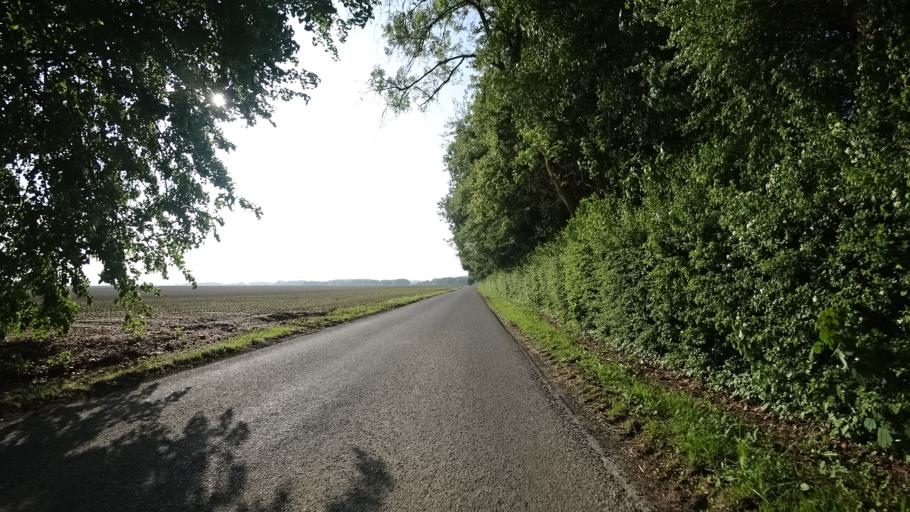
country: BE
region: Wallonia
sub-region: Province de Namur
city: Namur
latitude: 50.5355
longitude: 4.8142
